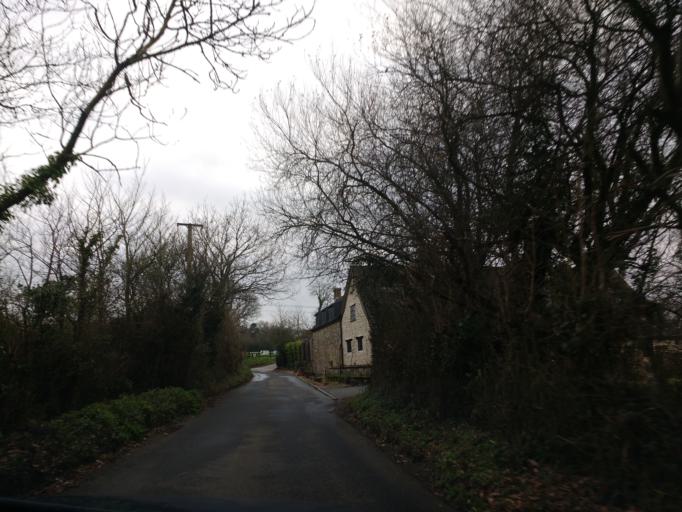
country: GB
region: England
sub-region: Isle of Wight
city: Shalfleet
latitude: 50.6982
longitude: -1.3938
